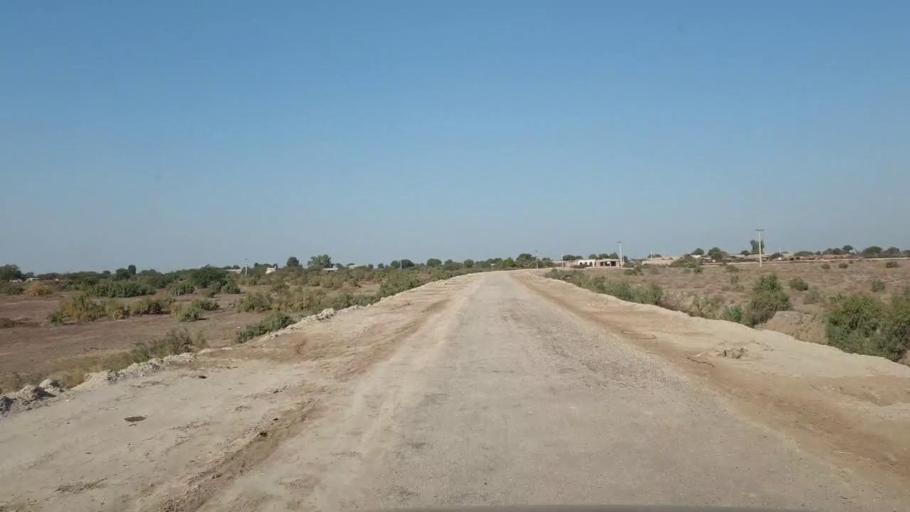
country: PK
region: Sindh
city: Shahpur Chakar
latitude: 26.1549
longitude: 68.6760
